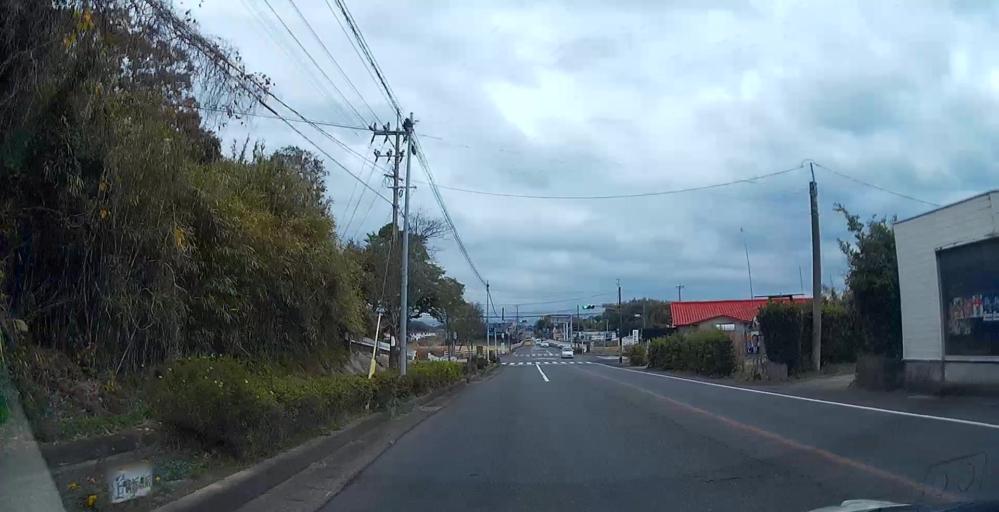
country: JP
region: Kagoshima
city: Akune
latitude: 32.0839
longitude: 130.1978
